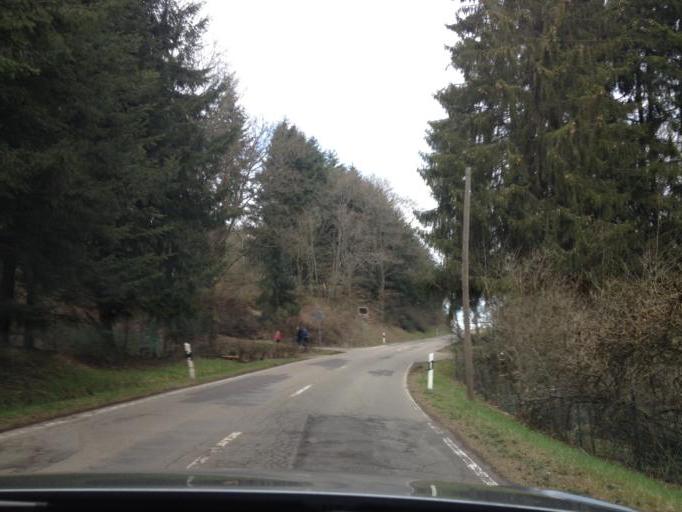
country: DE
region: Saarland
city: Freisen
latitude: 49.5609
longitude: 7.2427
